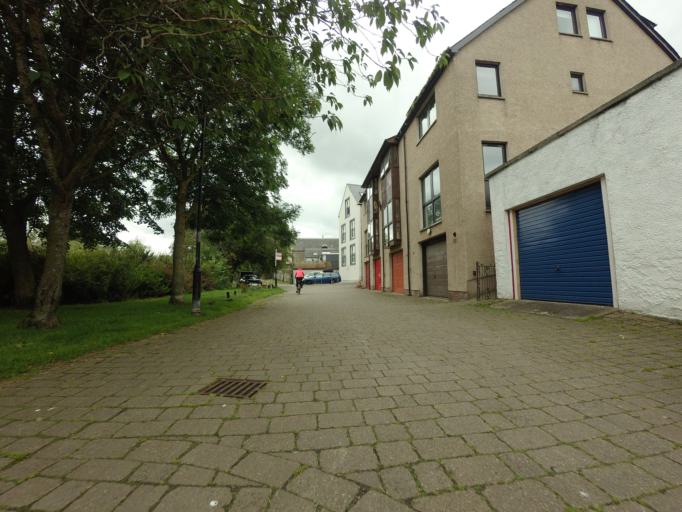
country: GB
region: Scotland
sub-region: Highland
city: Nairn
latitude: 57.5866
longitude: -3.8644
